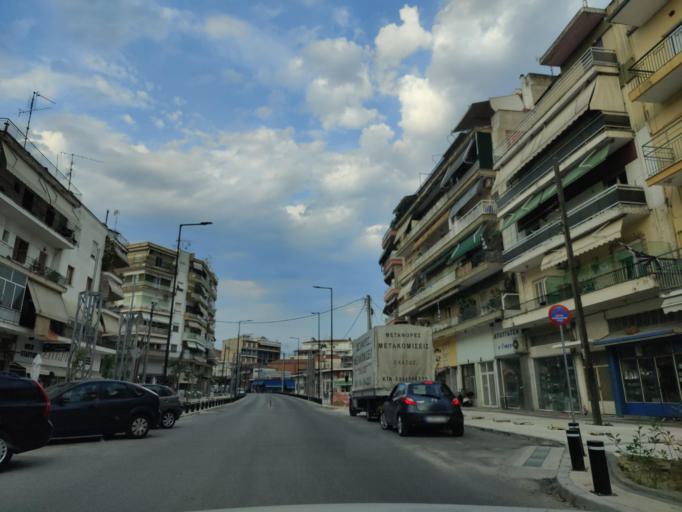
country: GR
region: East Macedonia and Thrace
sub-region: Nomos Dramas
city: Drama
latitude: 41.1485
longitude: 24.1432
